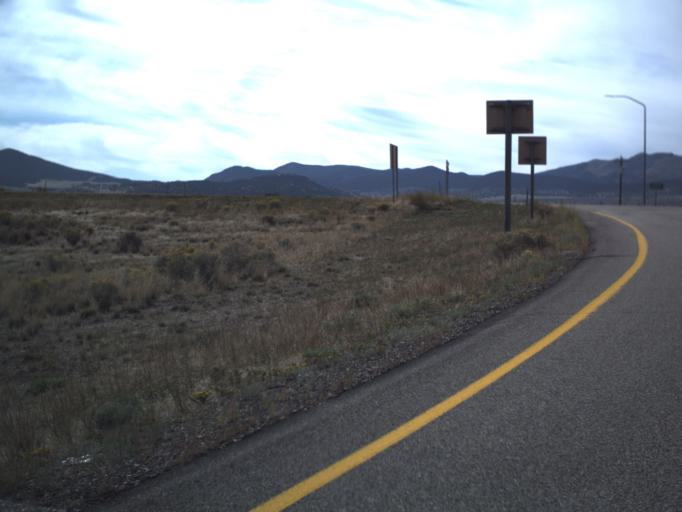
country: US
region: Utah
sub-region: Beaver County
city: Beaver
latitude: 38.2501
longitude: -112.6517
